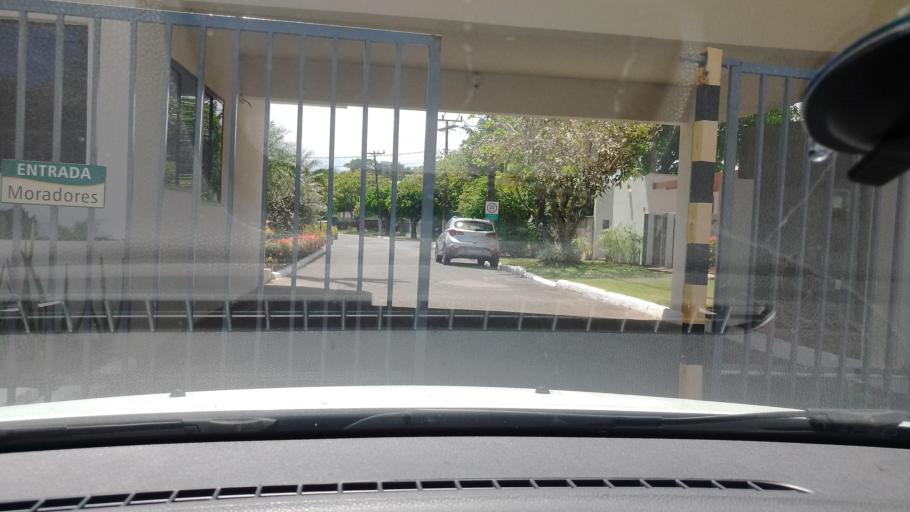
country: BR
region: Bahia
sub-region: Lauro De Freitas
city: Lauro de Freitas
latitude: -12.9542
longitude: -38.3925
